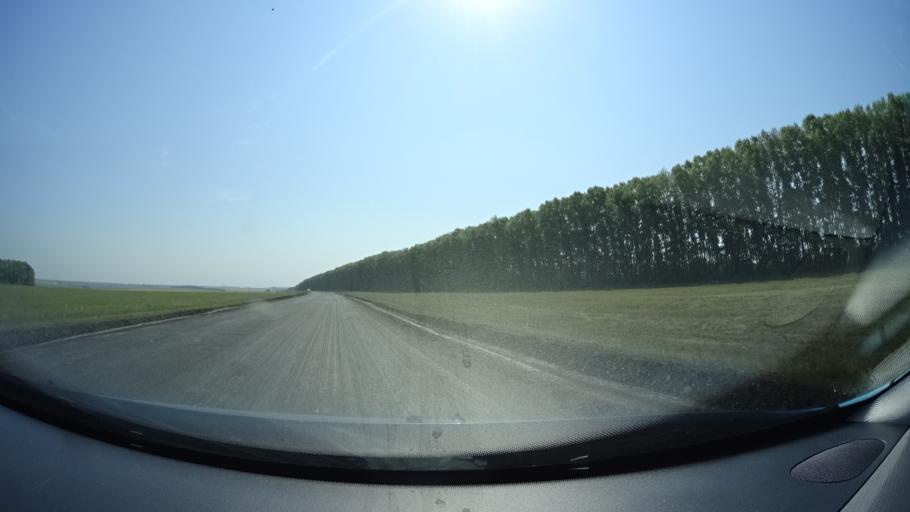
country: RU
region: Bashkortostan
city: Kabakovo
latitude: 54.4508
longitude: 55.9749
